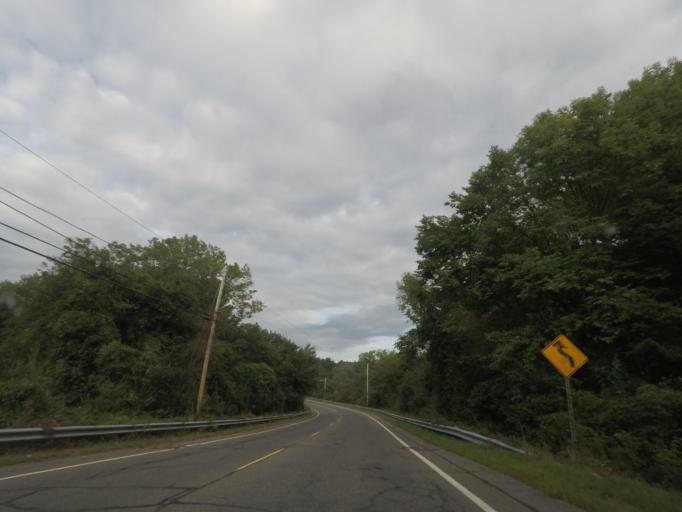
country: US
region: Massachusetts
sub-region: Hampden County
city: Palmer
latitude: 42.1908
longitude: -72.2868
